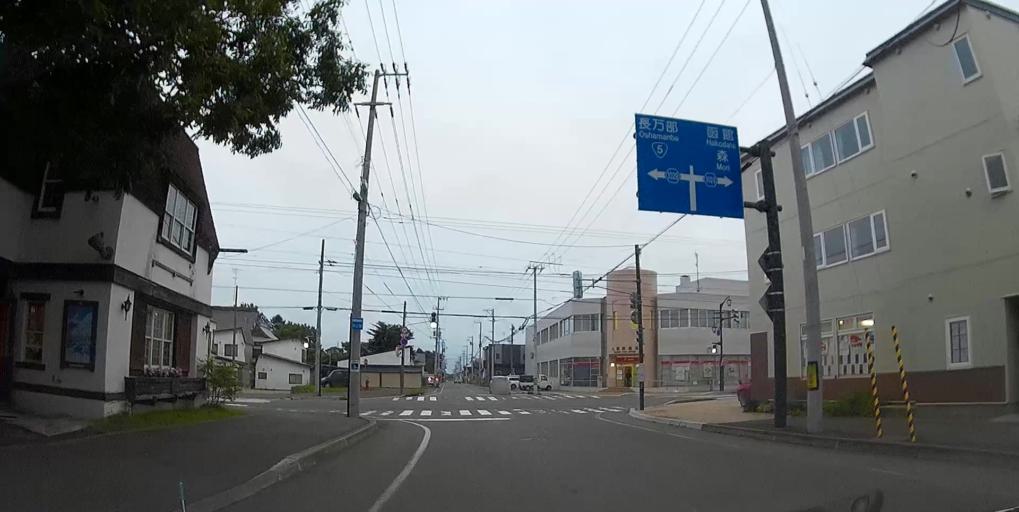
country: JP
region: Hokkaido
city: Nanae
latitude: 42.2571
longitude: 140.2681
